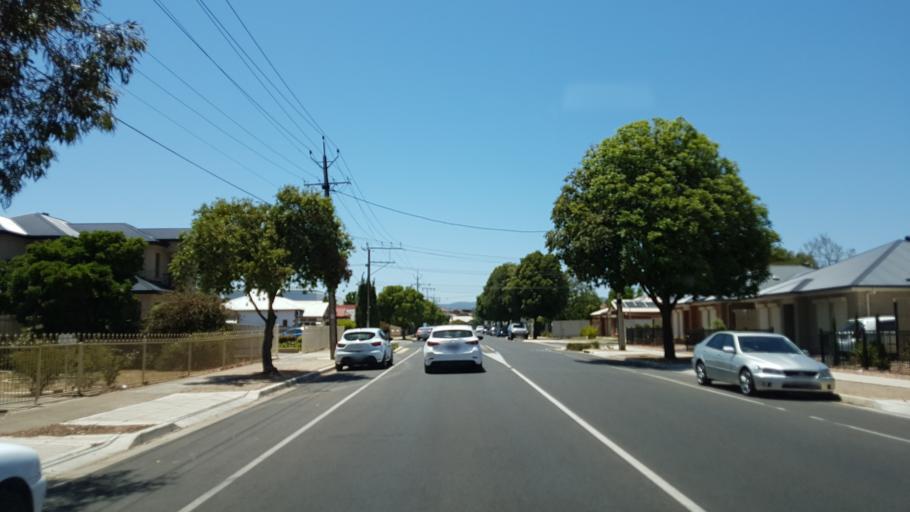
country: AU
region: South Australia
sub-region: Unley
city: Forestville
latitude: -34.9494
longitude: 138.5689
